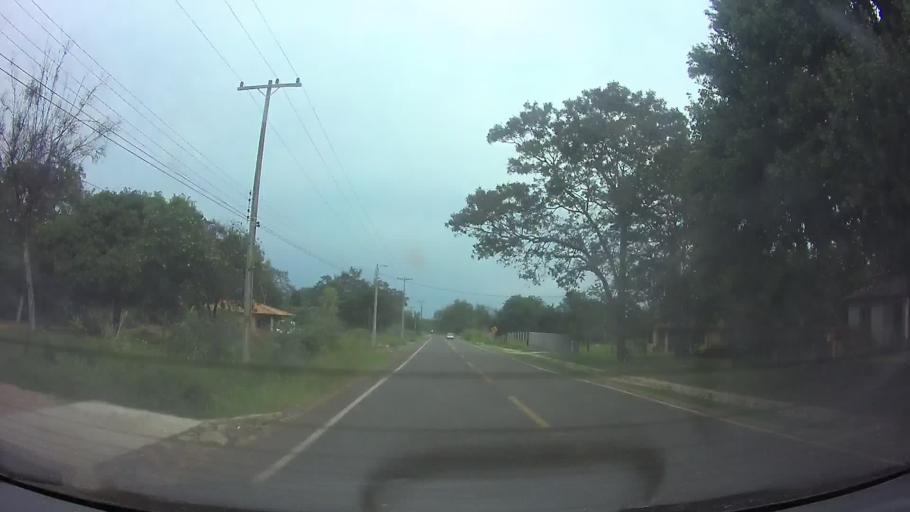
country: PY
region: Central
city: Limpio
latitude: -25.2118
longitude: -57.4796
